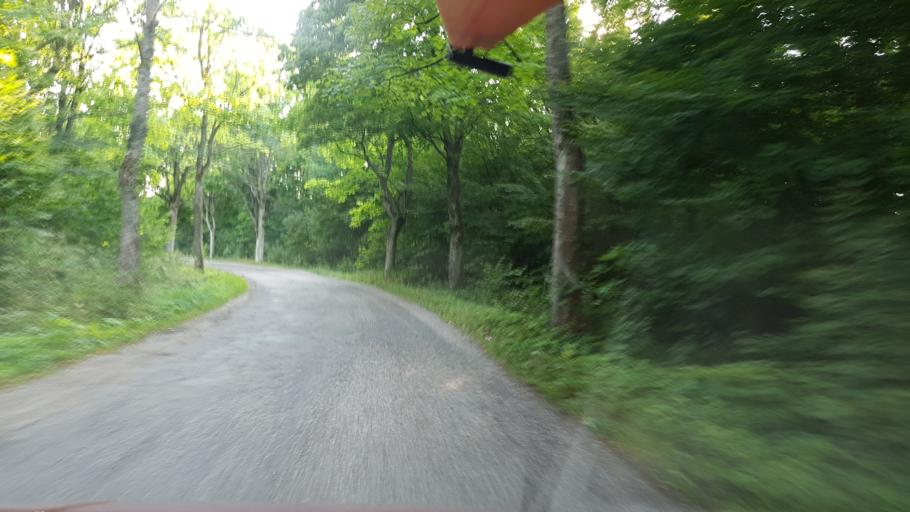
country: PL
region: West Pomeranian Voivodeship
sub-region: Powiat szczecinecki
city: Bialy Bor
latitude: 53.9799
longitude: 16.8692
